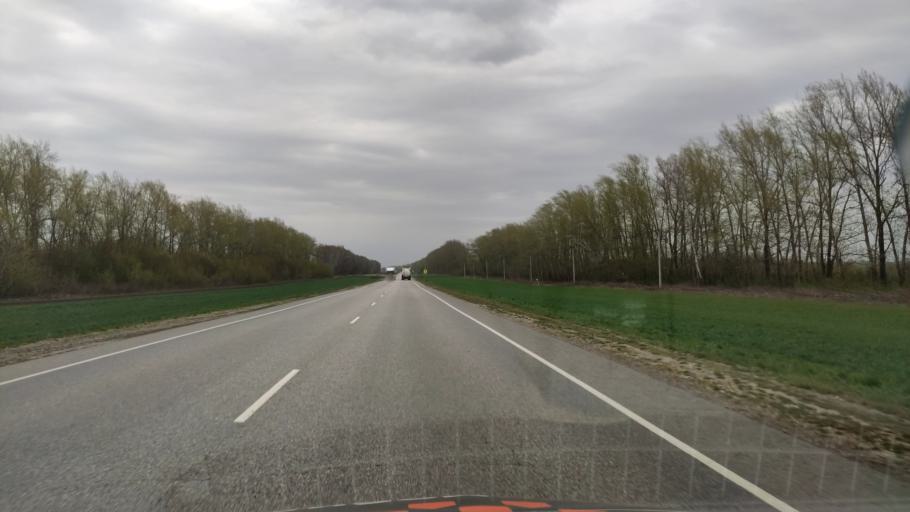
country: RU
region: Kursk
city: Olym
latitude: 51.5499
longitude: 38.1747
